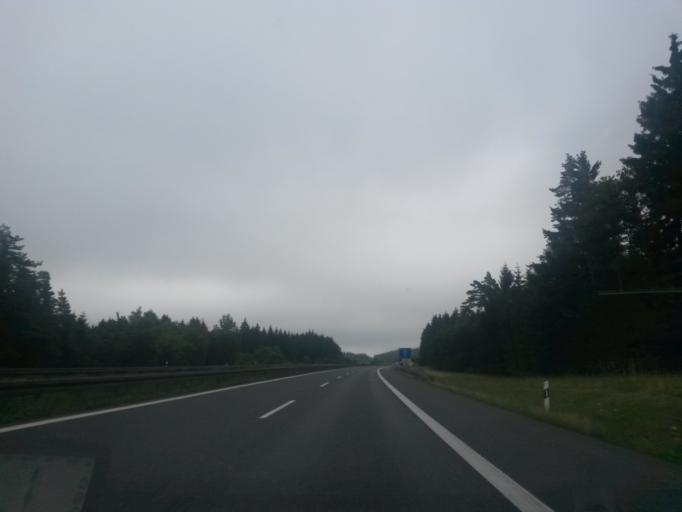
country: DE
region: Bavaria
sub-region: Upper Palatinate
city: Illschwang
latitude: 49.4254
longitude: 11.6785
